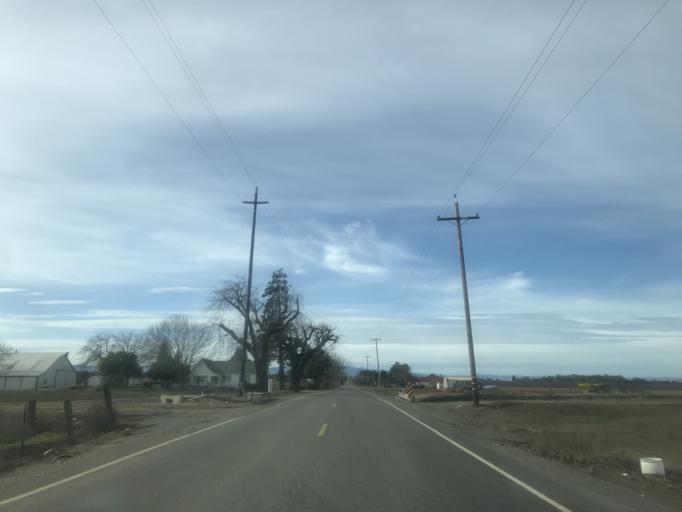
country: US
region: California
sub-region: Yolo County
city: Woodland
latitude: 38.6634
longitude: -121.8431
